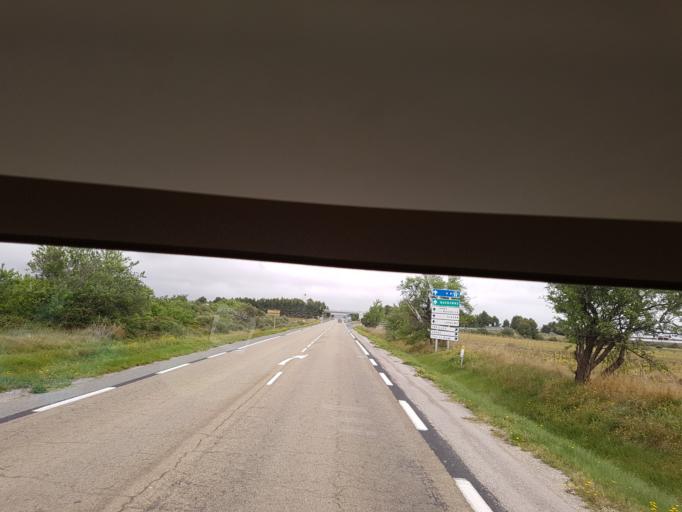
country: FR
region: Languedoc-Roussillon
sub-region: Departement de l'Aude
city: Leucate
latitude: 42.9289
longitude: 2.9935
